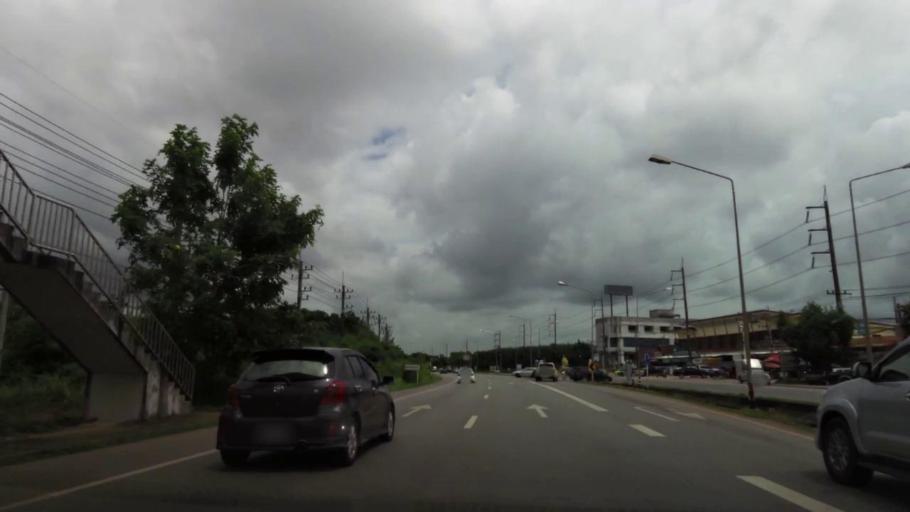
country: TH
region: Chanthaburi
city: Na Yai Am
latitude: 12.7661
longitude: 101.8510
